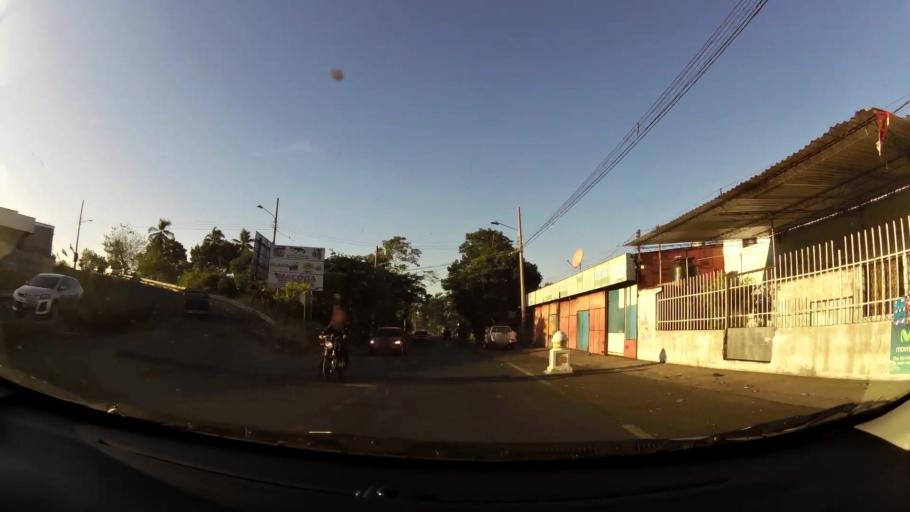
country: SV
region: Sonsonate
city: Sonsonate
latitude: 13.7097
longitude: -89.7288
